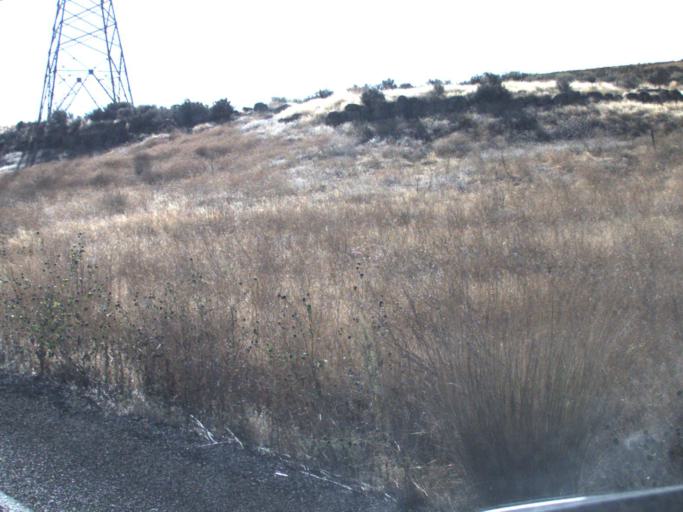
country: US
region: Washington
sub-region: Franklin County
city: Connell
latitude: 46.6292
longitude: -118.7264
